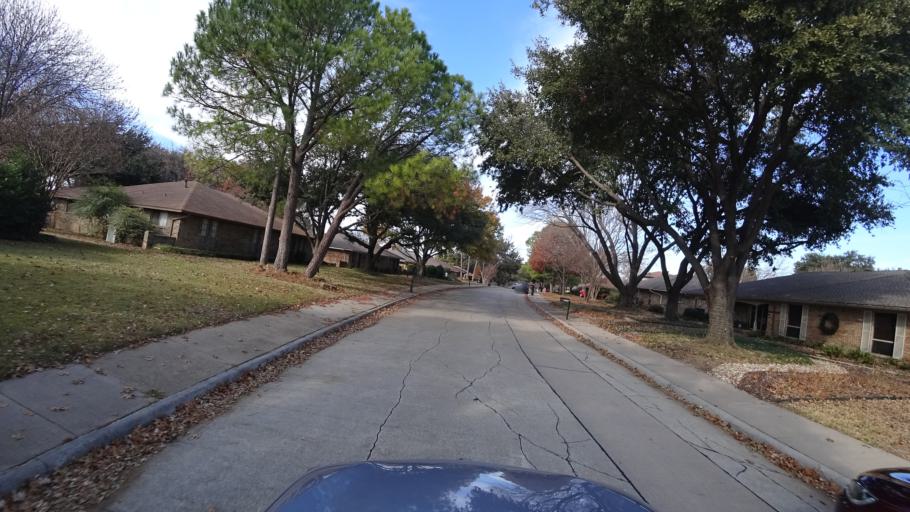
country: US
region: Texas
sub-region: Denton County
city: Lewisville
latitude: 33.0502
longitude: -97.0272
